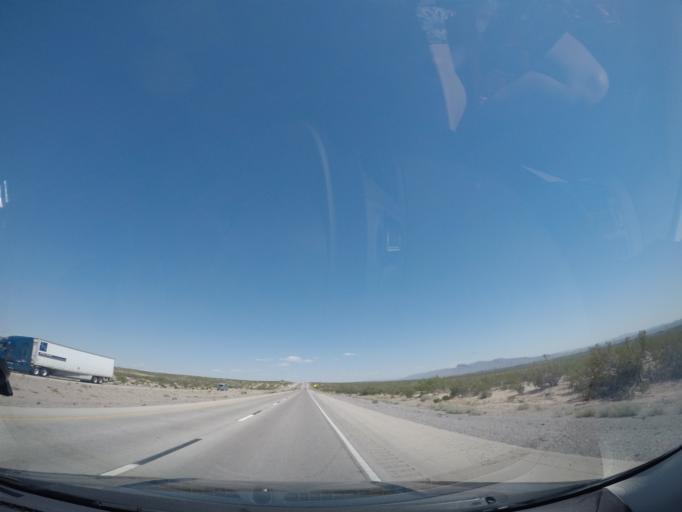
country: US
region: Texas
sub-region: El Paso County
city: Tornillo
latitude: 31.4528
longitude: -106.0399
